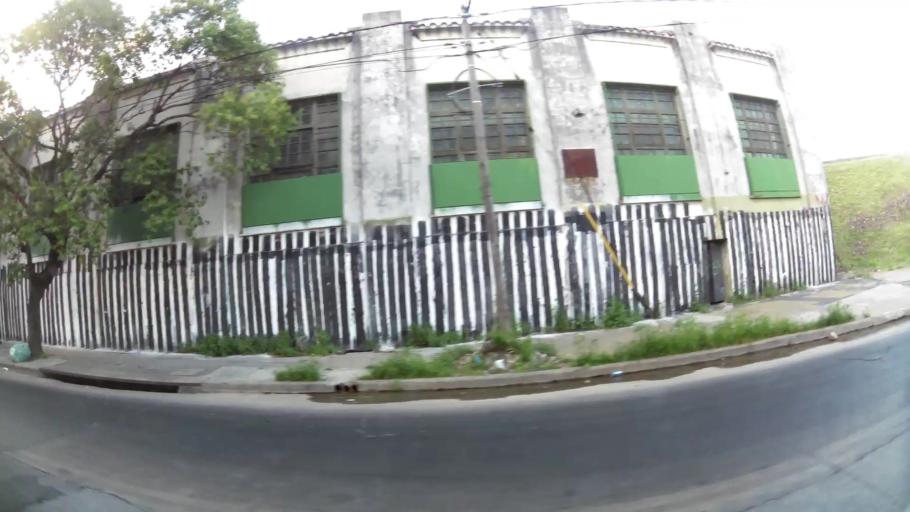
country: AR
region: Buenos Aires
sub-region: Partido de General San Martin
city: General San Martin
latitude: -34.5446
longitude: -58.4970
